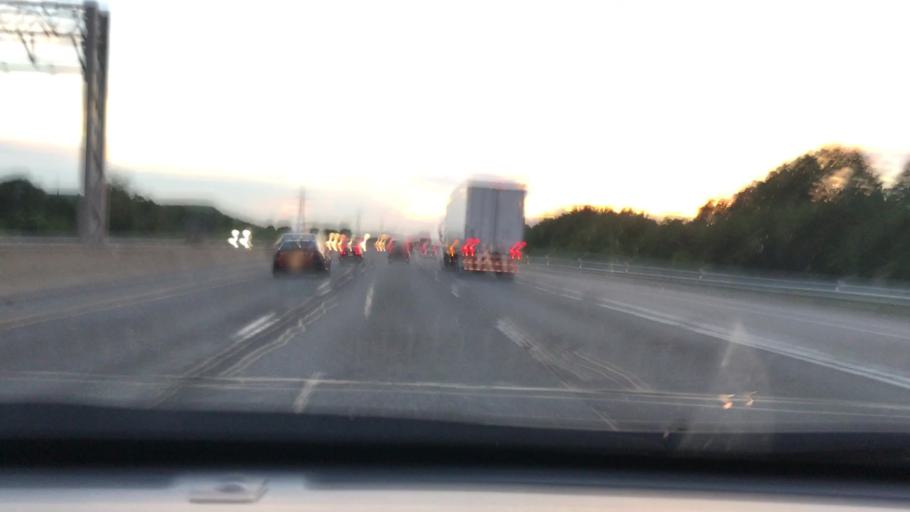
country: CA
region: Ontario
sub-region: Regional Municipality of Niagara
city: St. Catharines
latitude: 43.1902
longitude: -79.5241
